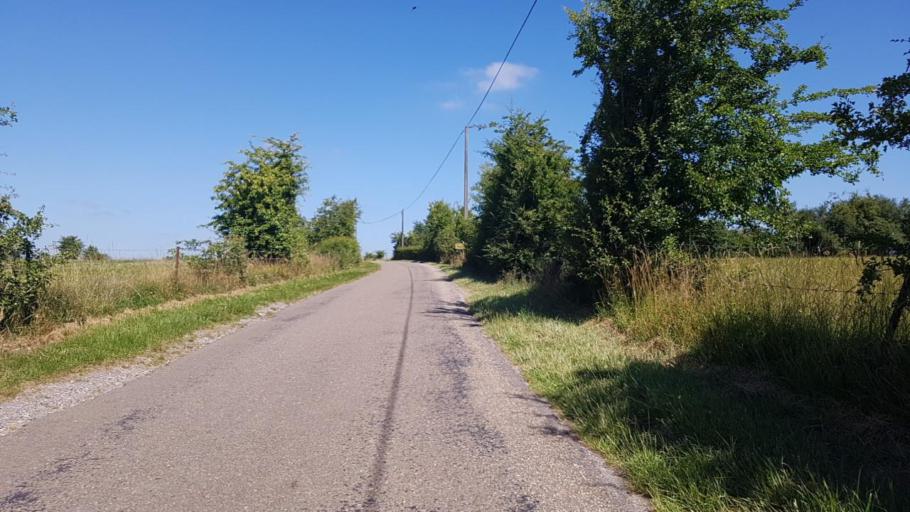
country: BE
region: Wallonia
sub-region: Province du Hainaut
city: Chimay
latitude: 50.0620
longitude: 4.2420
